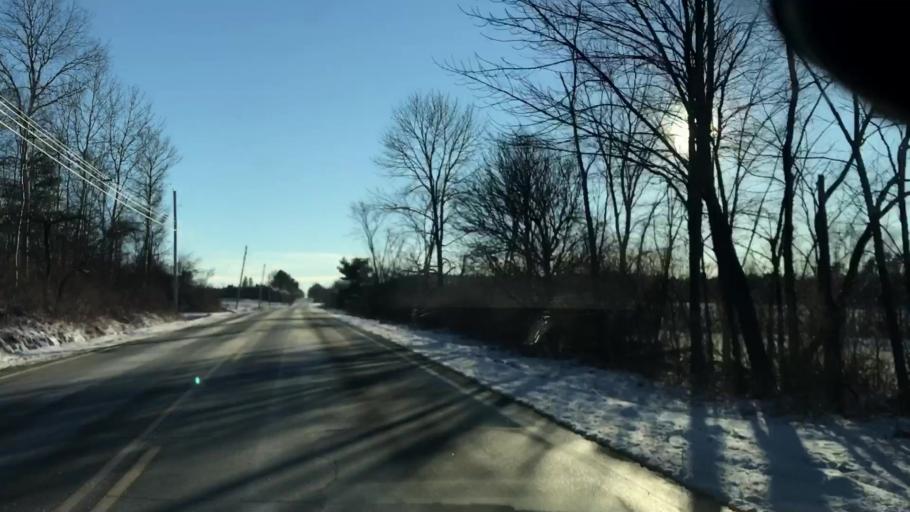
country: US
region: New Hampshire
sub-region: Grafton County
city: Haverhill
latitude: 44.0066
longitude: -72.0715
